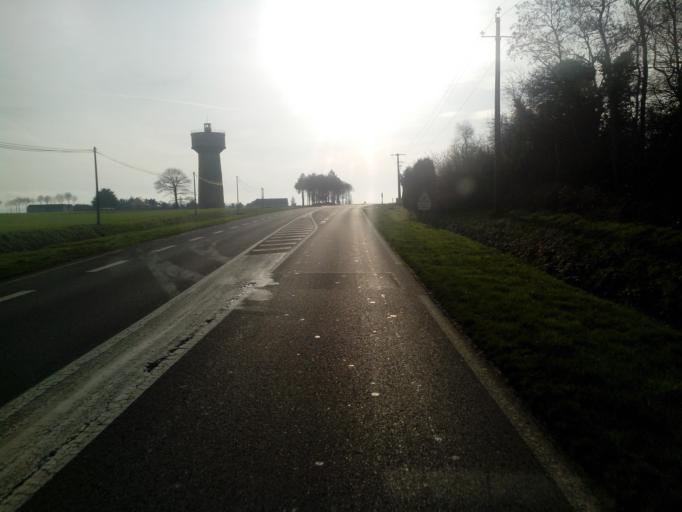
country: FR
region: Brittany
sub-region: Departement d'Ille-et-Vilaine
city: Gael
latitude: 48.1441
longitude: -2.2183
